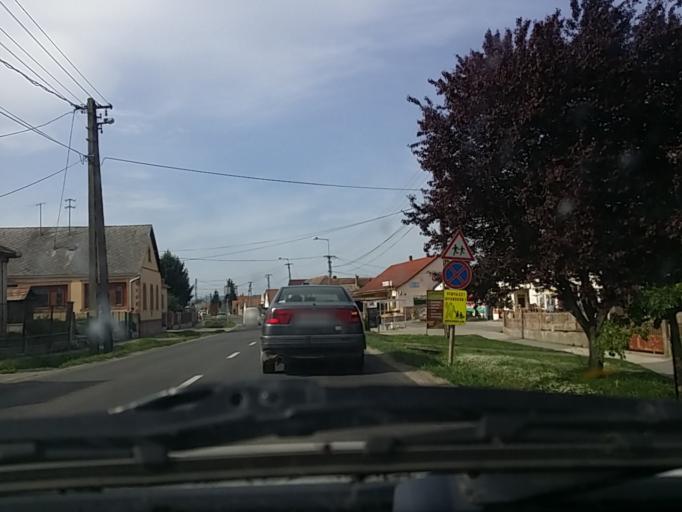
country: HU
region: Baranya
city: Kozarmisleny
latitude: 45.9486
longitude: 18.2377
